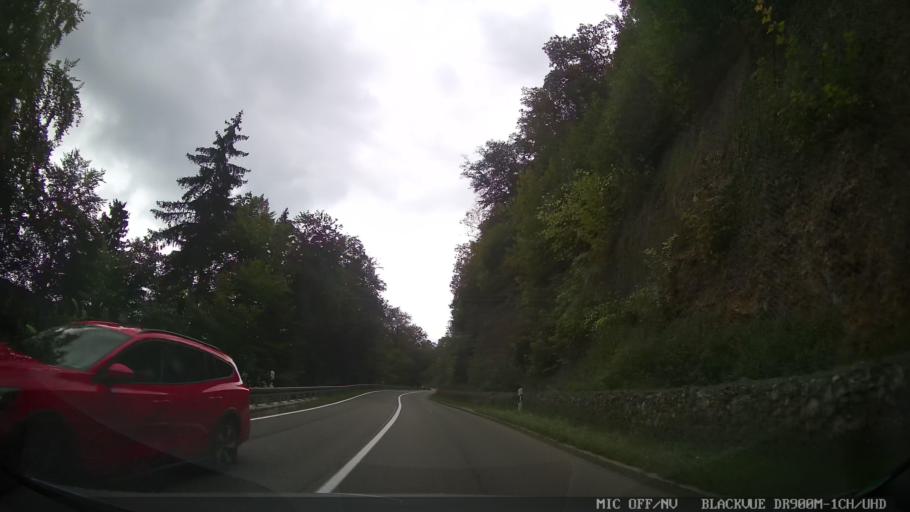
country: DE
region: Baden-Wuerttemberg
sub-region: Freiburg Region
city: Fridingen an der Donau
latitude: 48.0141
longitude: 8.9159
